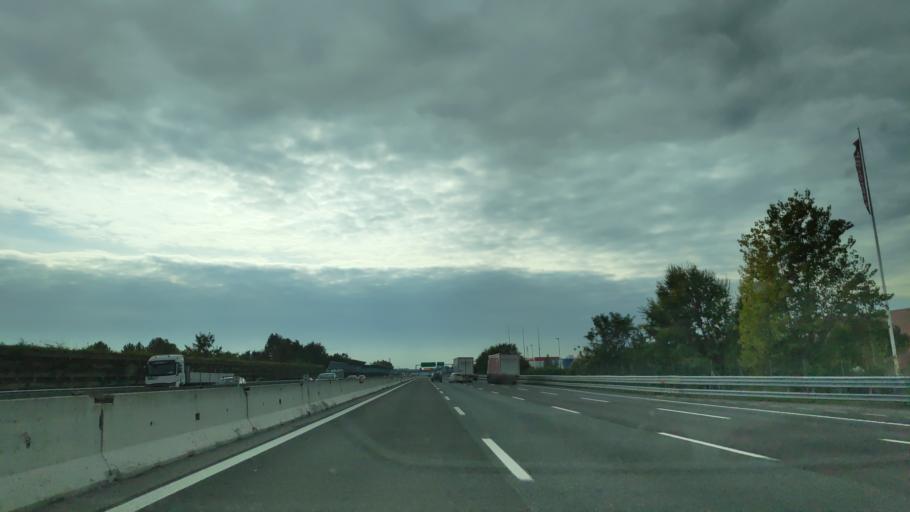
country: IT
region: Lombardy
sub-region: Provincia di Bergamo
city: Lallio
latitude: 45.6541
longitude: 9.6380
